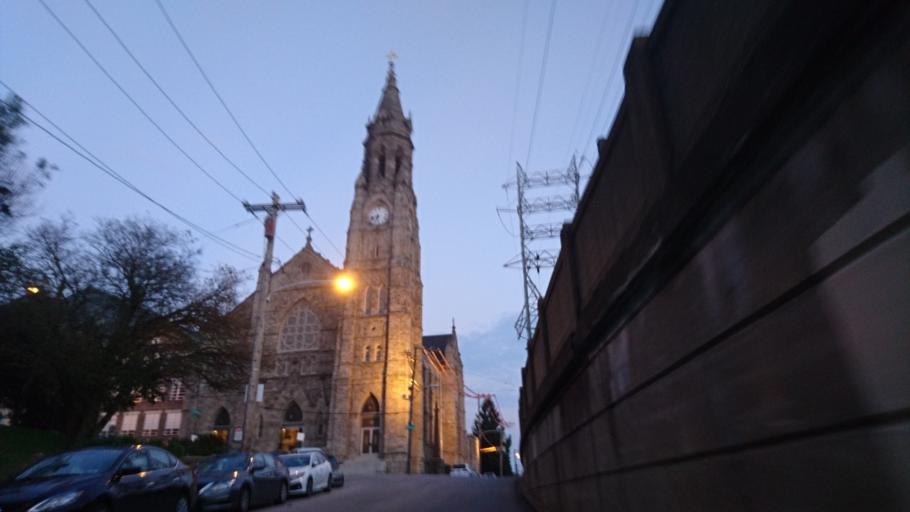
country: US
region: Pennsylvania
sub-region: Montgomery County
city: Bala-Cynwyd
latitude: 40.0252
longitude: -75.2212
